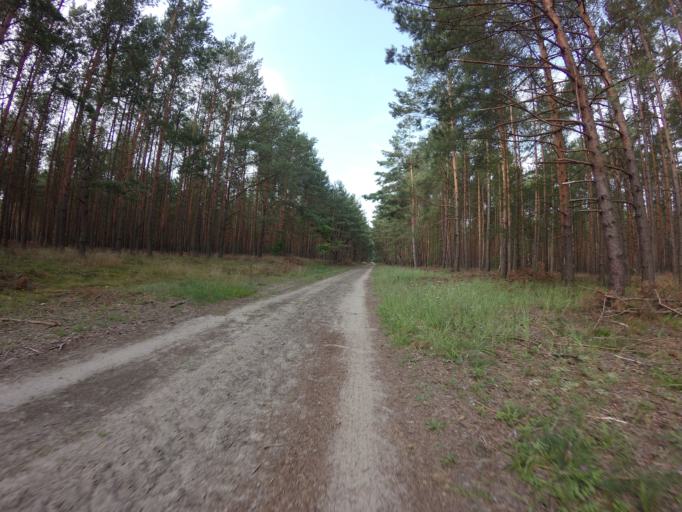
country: PL
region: Kujawsko-Pomorskie
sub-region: Powiat bydgoski
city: Osielsko
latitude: 53.1512
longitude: 18.0905
